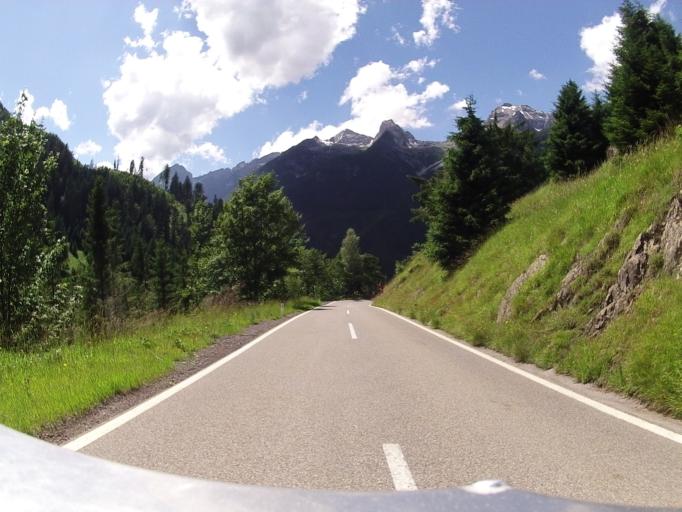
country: AT
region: Tyrol
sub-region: Politischer Bezirk Reutte
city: Elmen
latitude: 47.3243
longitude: 10.5333
